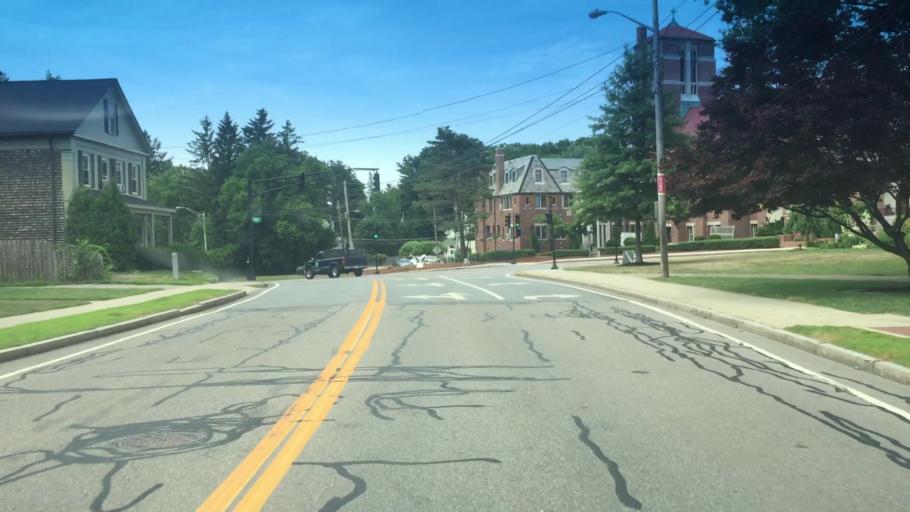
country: US
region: Massachusetts
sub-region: Norfolk County
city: Franklin
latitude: 42.0890
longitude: -71.4020
